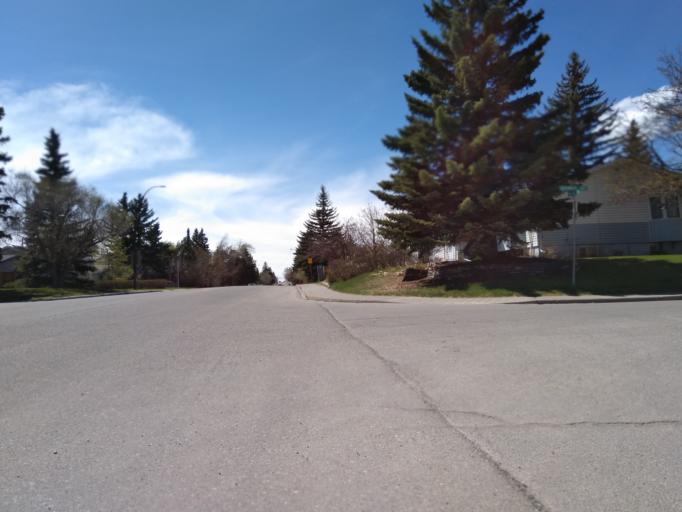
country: CA
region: Alberta
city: Calgary
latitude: 51.0126
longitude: -114.1438
